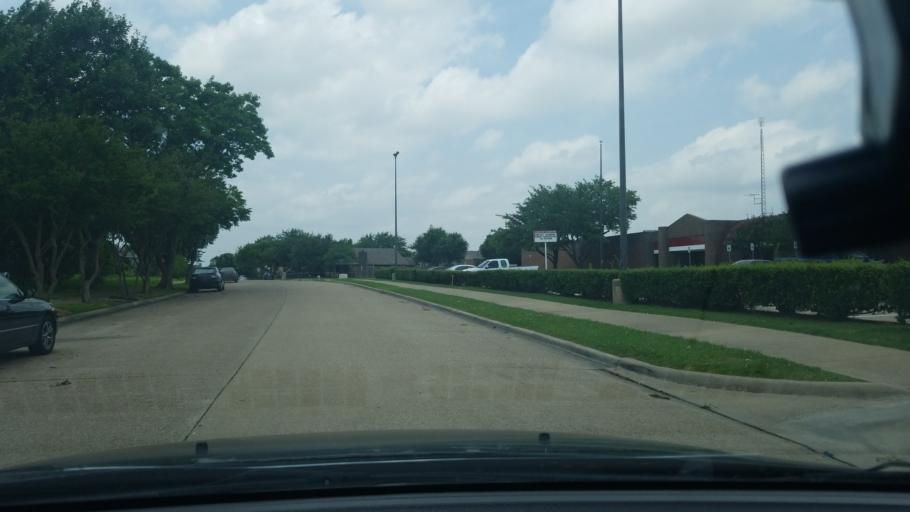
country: US
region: Texas
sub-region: Dallas County
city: Mesquite
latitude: 32.8028
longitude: -96.6170
